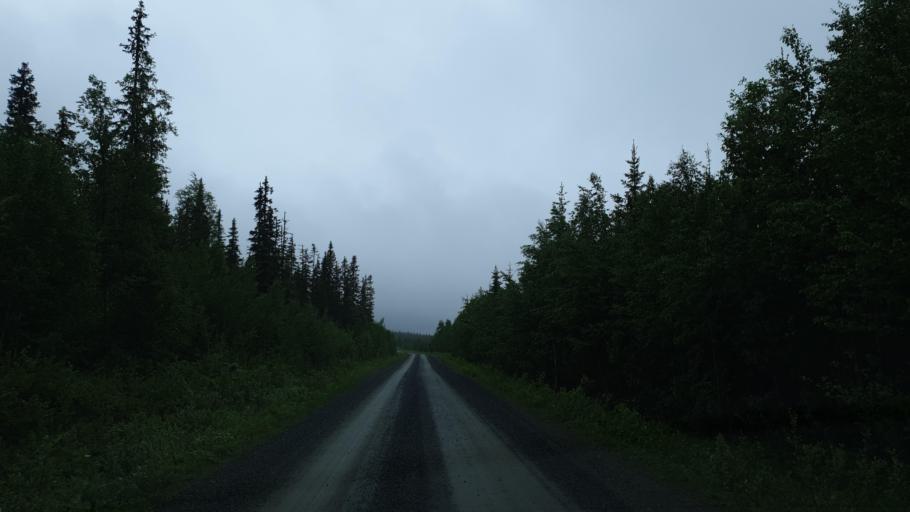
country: SE
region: Vaesterbotten
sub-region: Vilhelmina Kommun
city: Sjoberg
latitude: 65.3248
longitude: 15.9293
